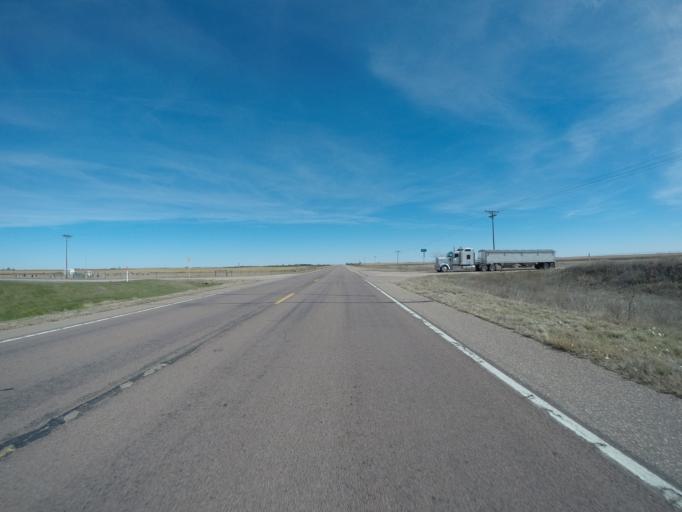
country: US
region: Colorado
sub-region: Yuma County
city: Yuma
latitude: 39.6559
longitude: -102.6503
